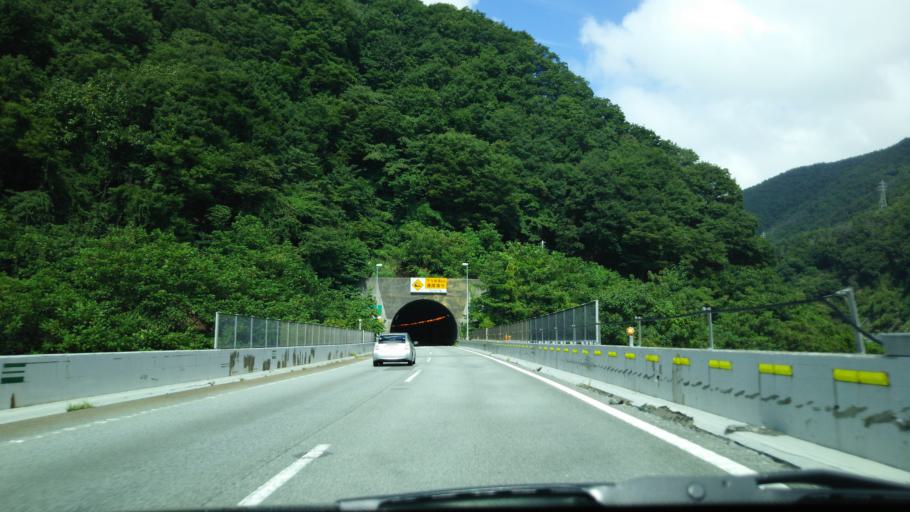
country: JP
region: Yamanashi
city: Enzan
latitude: 35.6441
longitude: 138.7648
